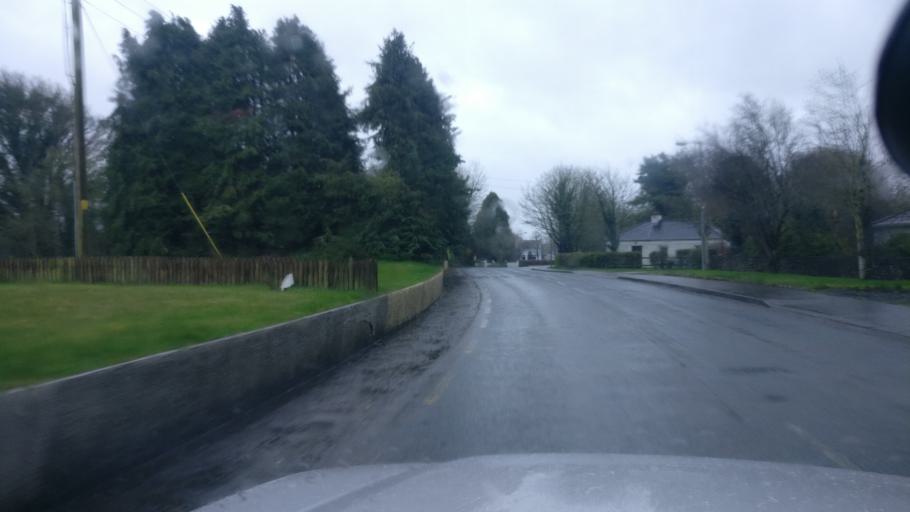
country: IE
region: Connaught
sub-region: County Galway
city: Ballinasloe
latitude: 53.2386
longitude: -8.1736
